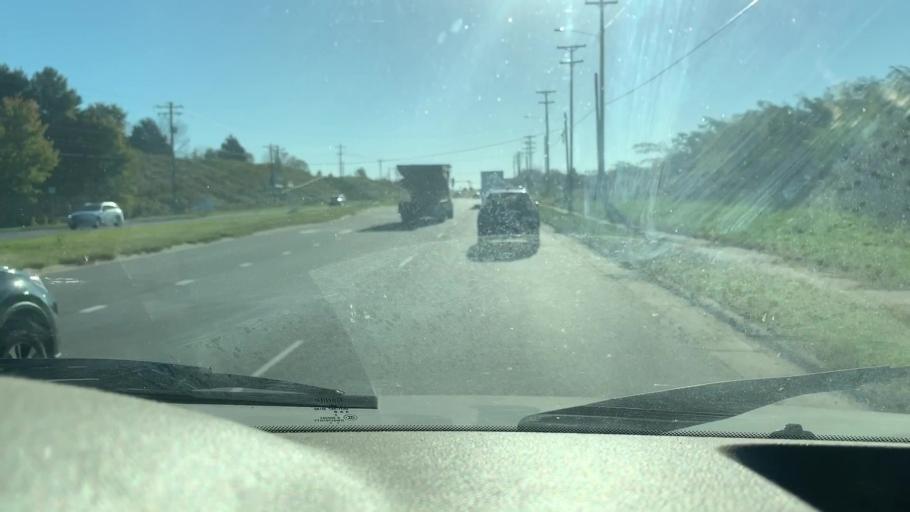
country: US
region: North Carolina
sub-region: Cabarrus County
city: Harrisburg
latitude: 35.4061
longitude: -80.7104
